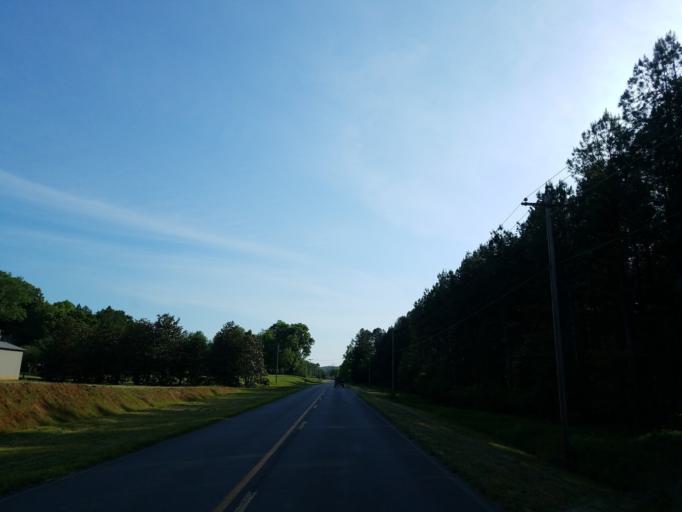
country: US
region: Georgia
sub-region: Chattooga County
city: Trion
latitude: 34.5777
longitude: -85.1512
